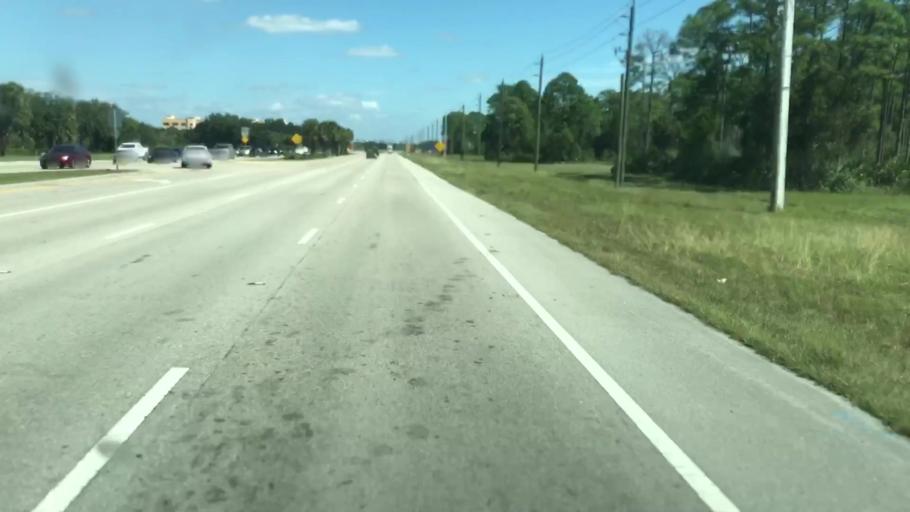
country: US
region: Florida
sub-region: Lee County
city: Gateway
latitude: 26.5533
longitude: -81.7547
